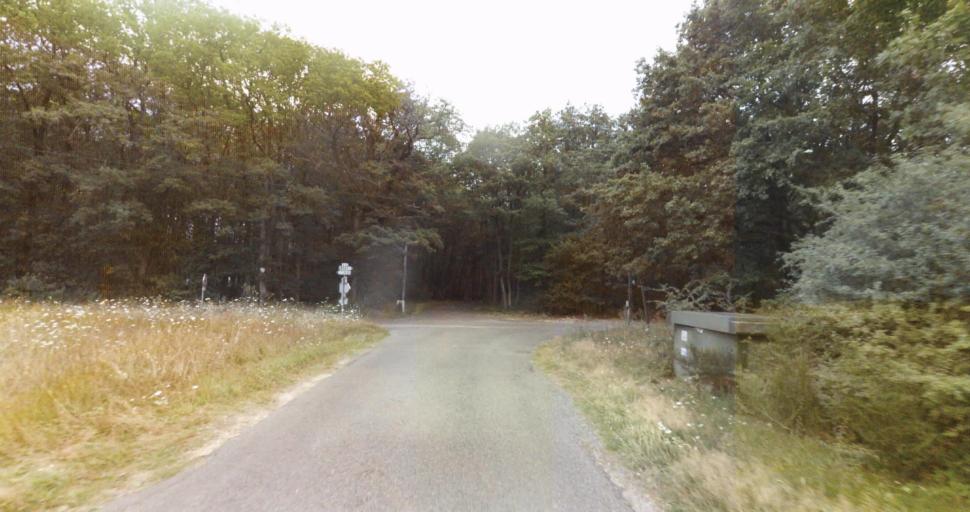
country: FR
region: Centre
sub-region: Departement d'Eure-et-Loir
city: Vert-en-Drouais
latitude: 48.7785
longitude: 1.3231
